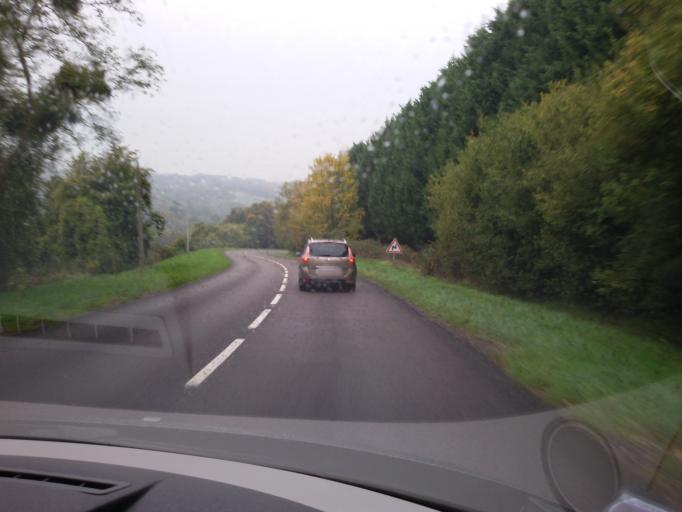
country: FR
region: Lower Normandy
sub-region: Departement du Calvados
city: Houlgate
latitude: 49.2996
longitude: -0.0418
